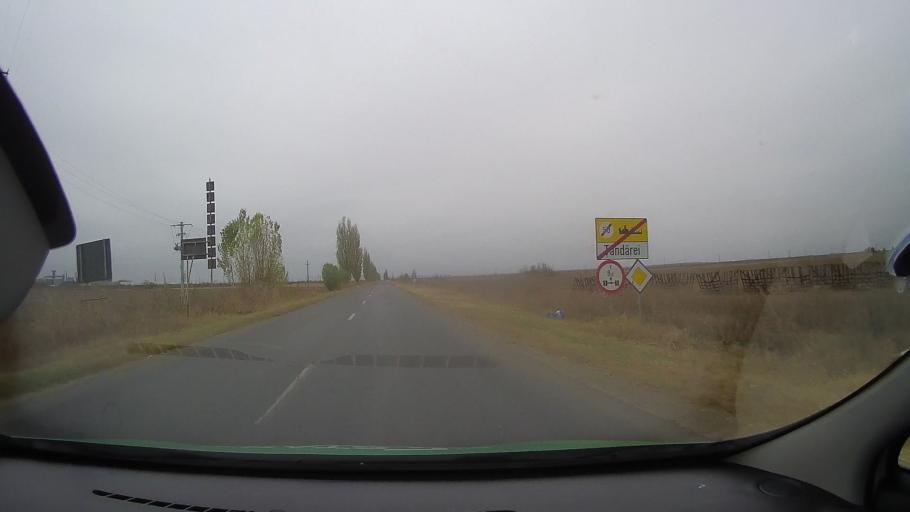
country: RO
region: Ialomita
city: Tandarei
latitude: 44.6560
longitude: 27.6523
